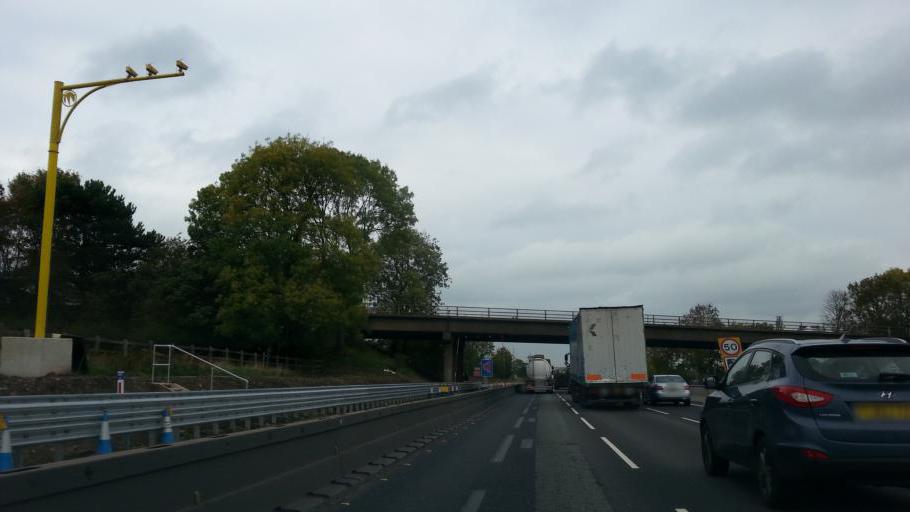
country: GB
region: England
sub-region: Cheshire East
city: Peover Superior
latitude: 53.2540
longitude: -2.4021
